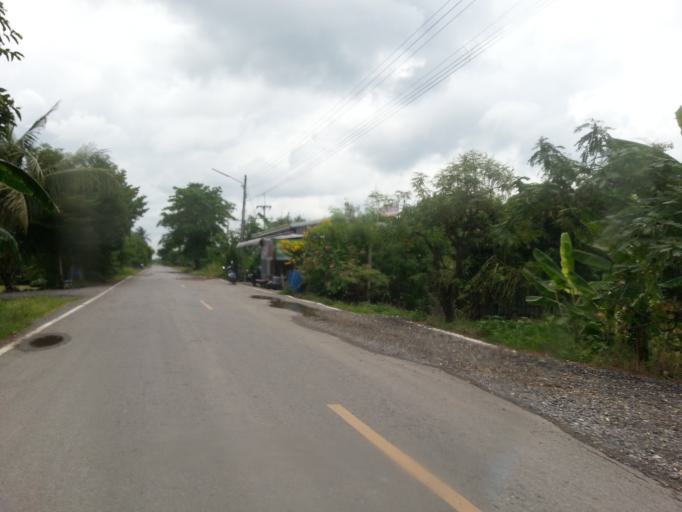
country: TH
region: Pathum Thani
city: Ban Lam Luk Ka
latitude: 14.0300
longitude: 100.8473
